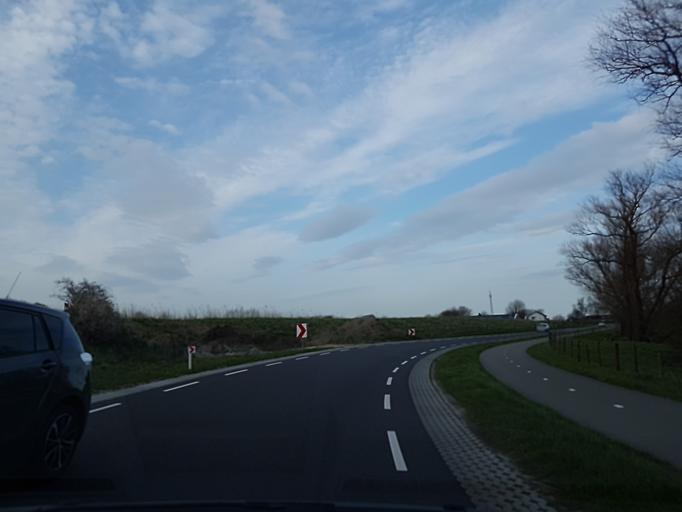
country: NL
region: Zeeland
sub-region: Gemeente Terneuzen
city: Sluiskil
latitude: 51.2980
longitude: 3.7725
